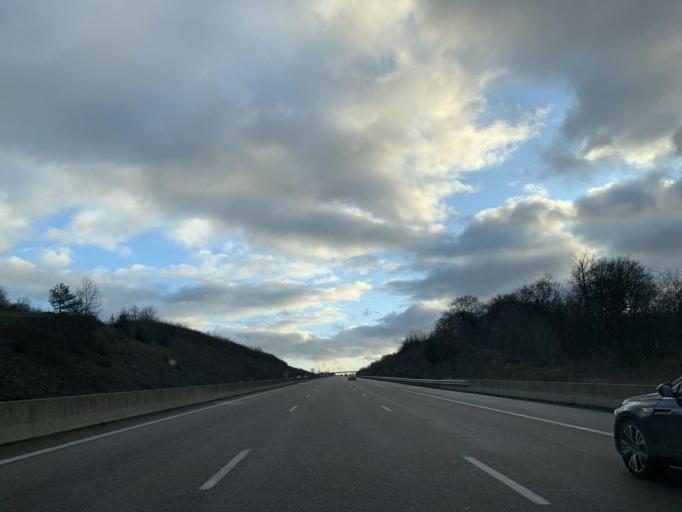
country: FR
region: Bourgogne
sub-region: Departement de la Cote-d'Or
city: Selongey
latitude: 47.7406
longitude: 5.1948
